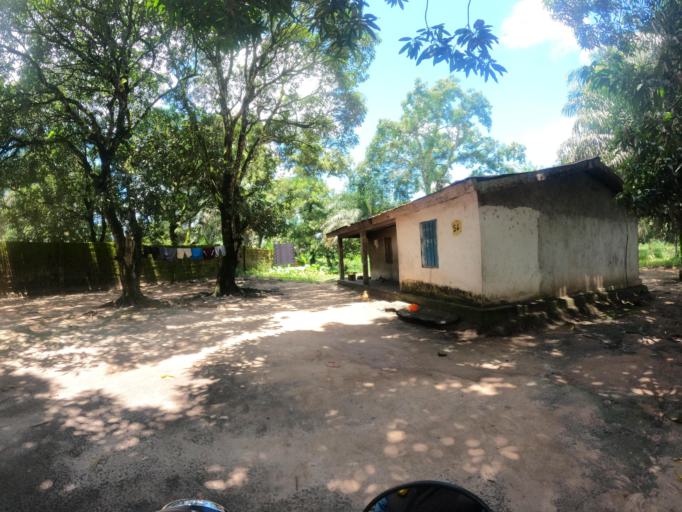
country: SL
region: Northern Province
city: Makeni
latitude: 8.8980
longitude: -12.0617
